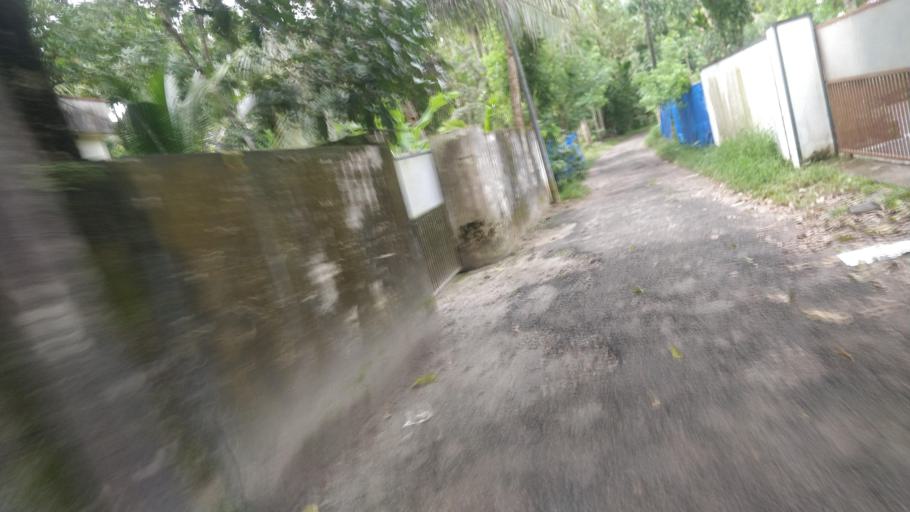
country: IN
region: Kerala
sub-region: Alappuzha
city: Shertallai
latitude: 9.6861
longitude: 76.3563
